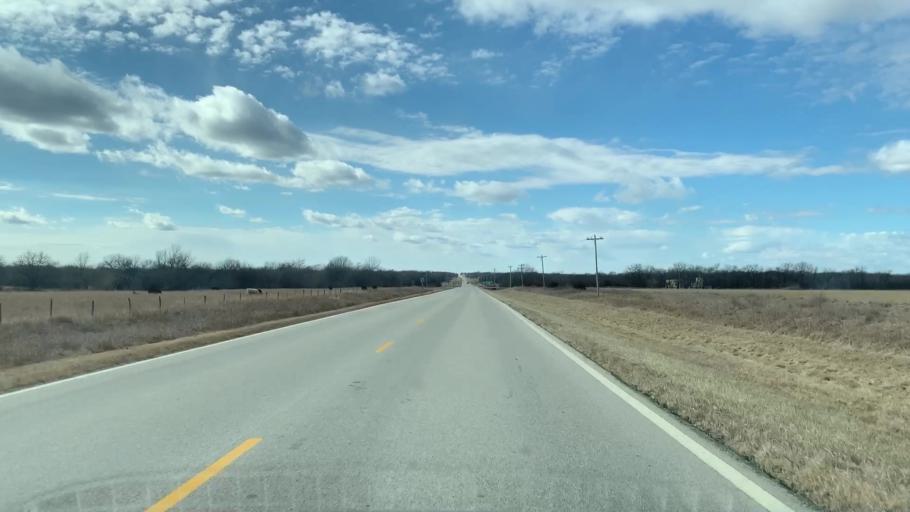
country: US
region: Kansas
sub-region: Neosho County
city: Erie
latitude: 37.5292
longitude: -95.3936
